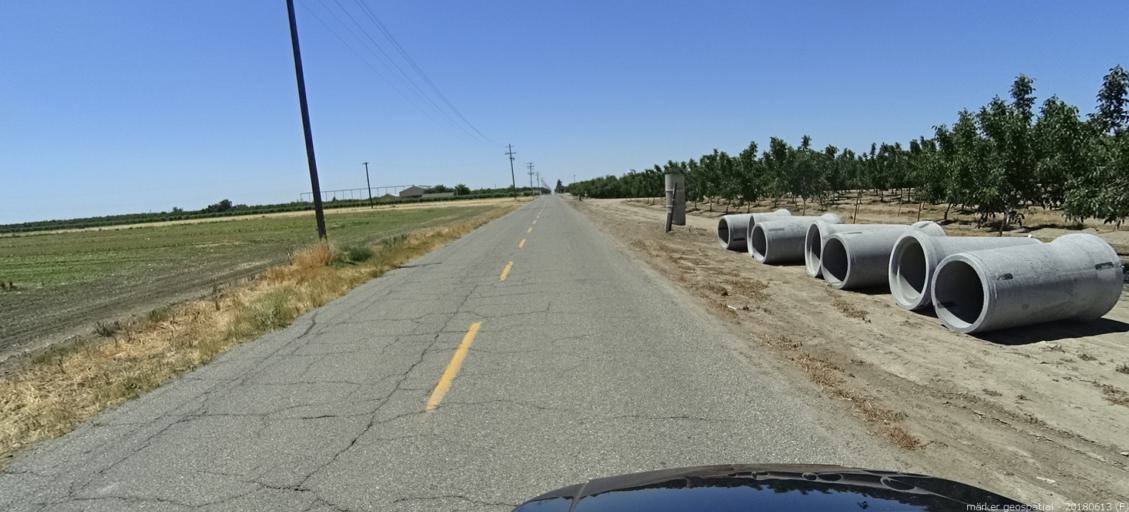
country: US
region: California
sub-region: Madera County
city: Chowchilla
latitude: 37.0375
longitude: -120.3106
